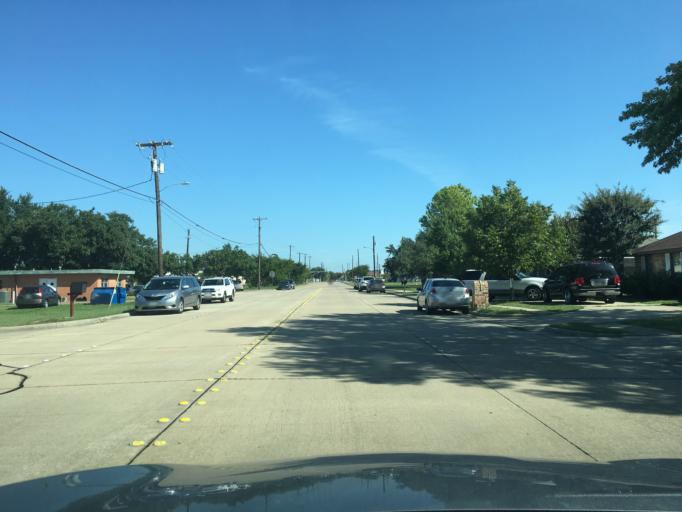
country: US
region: Texas
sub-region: Dallas County
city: Sachse
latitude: 32.9693
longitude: -96.6011
